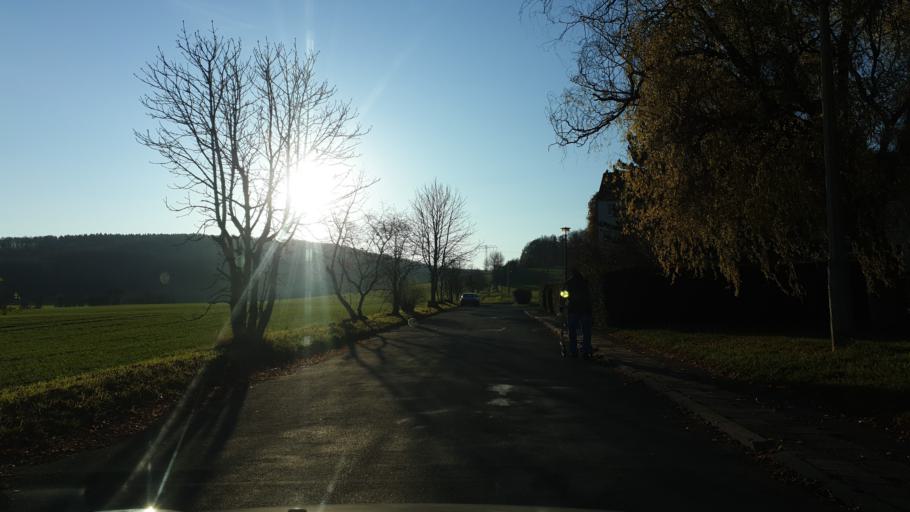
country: DE
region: Thuringia
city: Hartmannsdorf
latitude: 50.9727
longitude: 11.9716
